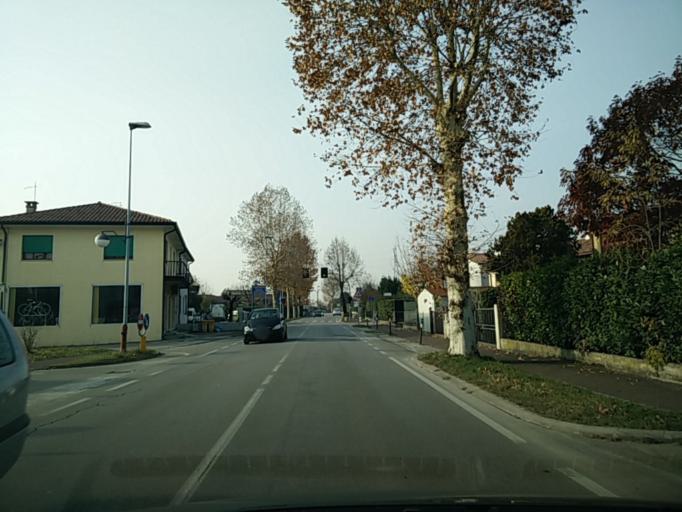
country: IT
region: Veneto
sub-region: Provincia di Treviso
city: Salvatronda
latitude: 45.6759
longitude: 11.9730
